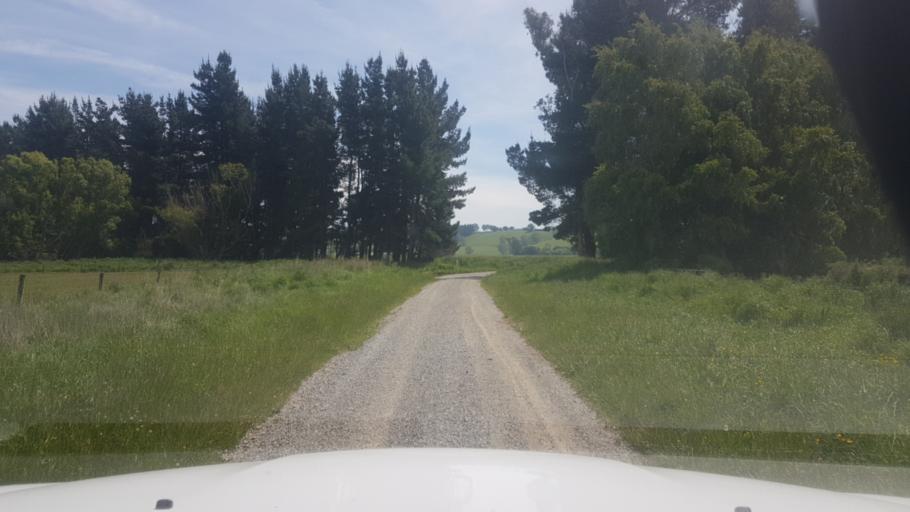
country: NZ
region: Canterbury
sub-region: Timaru District
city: Pleasant Point
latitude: -44.2209
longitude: 171.1627
